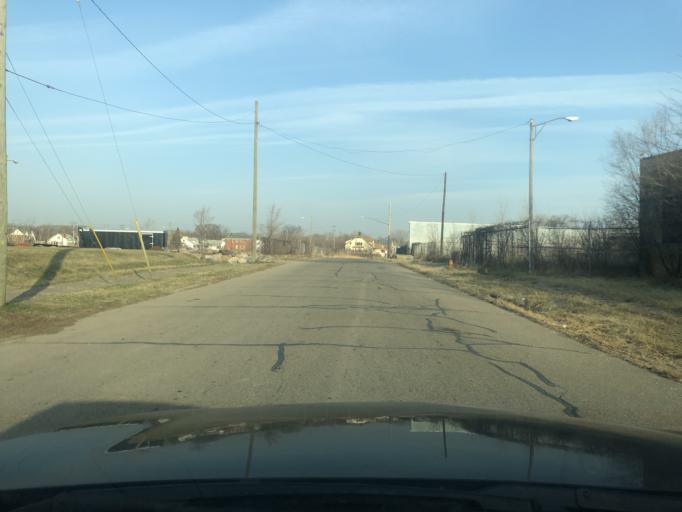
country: US
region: Michigan
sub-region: Wayne County
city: Highland Park
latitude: 42.3973
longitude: -83.1320
